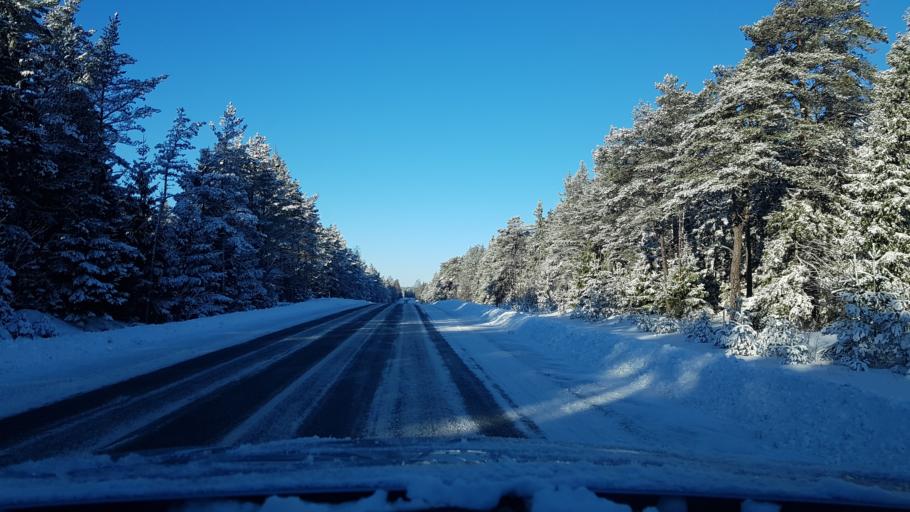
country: EE
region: Hiiumaa
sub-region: Kaerdla linn
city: Kardla
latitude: 58.9598
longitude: 22.8531
